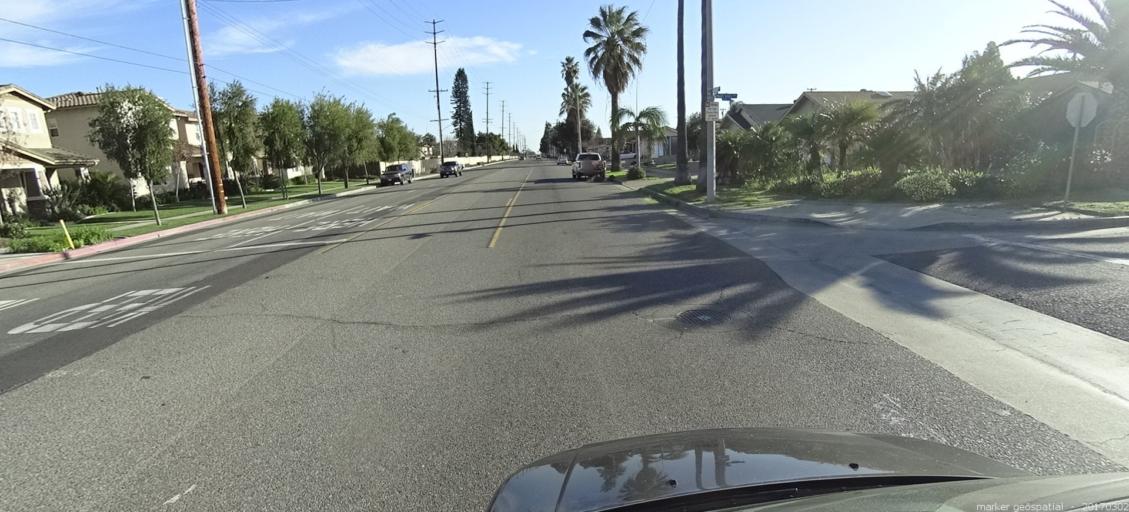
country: US
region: California
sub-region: Orange County
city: Placentia
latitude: 33.8434
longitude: -117.8717
